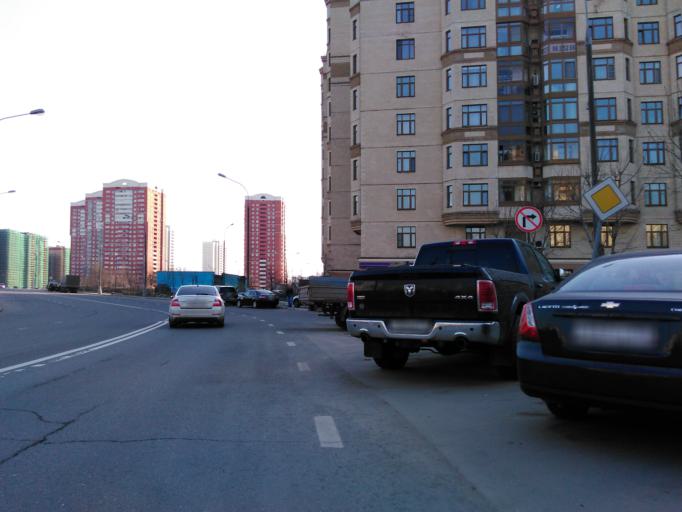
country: RU
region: Moscow
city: Ramenki
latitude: 55.7014
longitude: 37.5141
